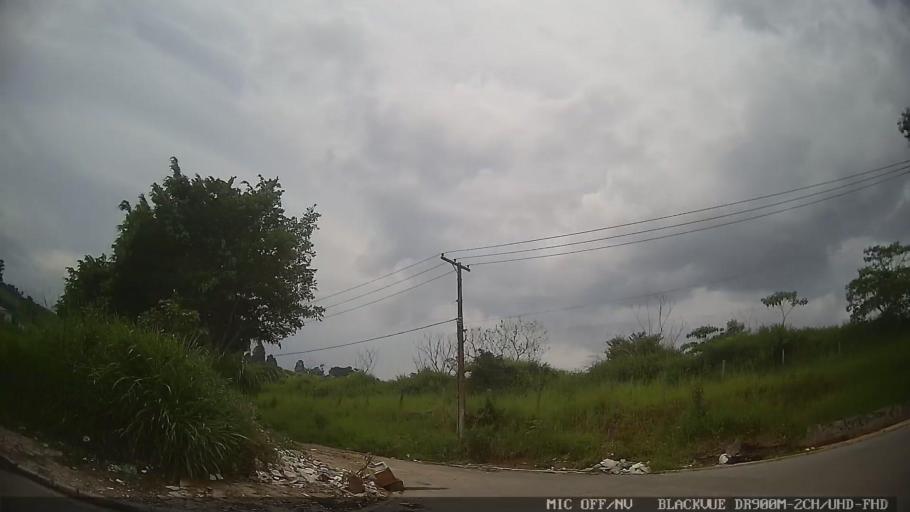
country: BR
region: Sao Paulo
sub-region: Itaquaquecetuba
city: Itaquaquecetuba
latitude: -23.4606
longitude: -46.3076
